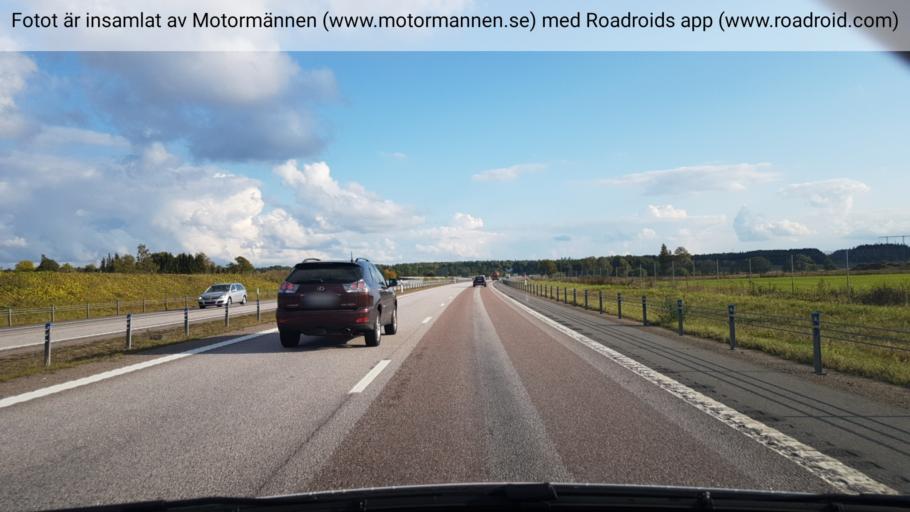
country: SE
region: Uppsala
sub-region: Tierps Kommun
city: Tierp
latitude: 60.3307
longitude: 17.5028
